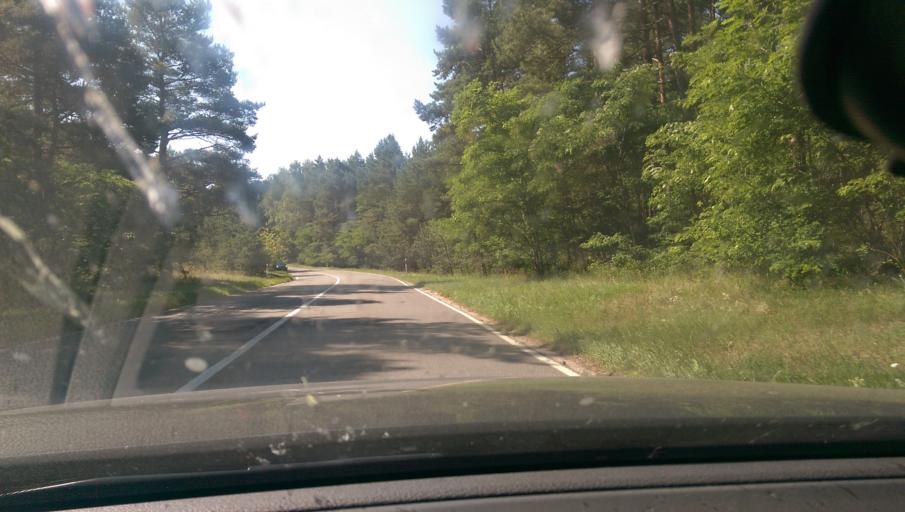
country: LT
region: Klaipedos apskritis
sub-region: Klaipeda
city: Klaipeda
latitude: 55.6632
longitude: 21.1162
